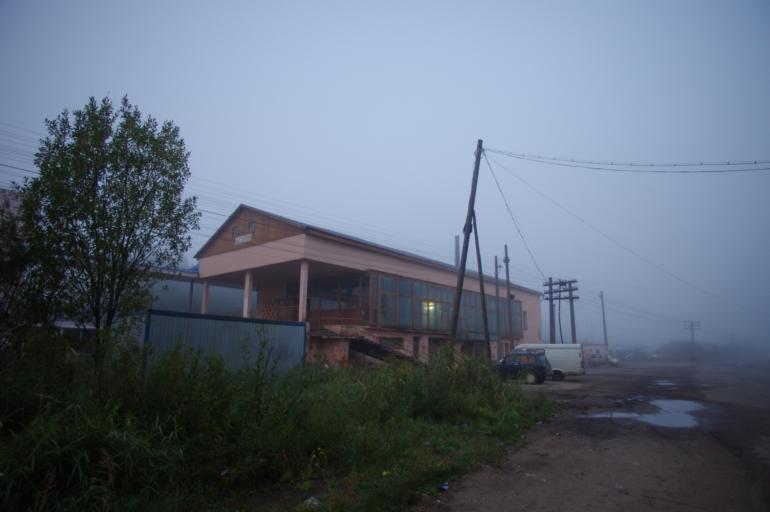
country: RU
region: Jaroslavl
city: Borok
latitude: 57.9318
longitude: 38.2387
